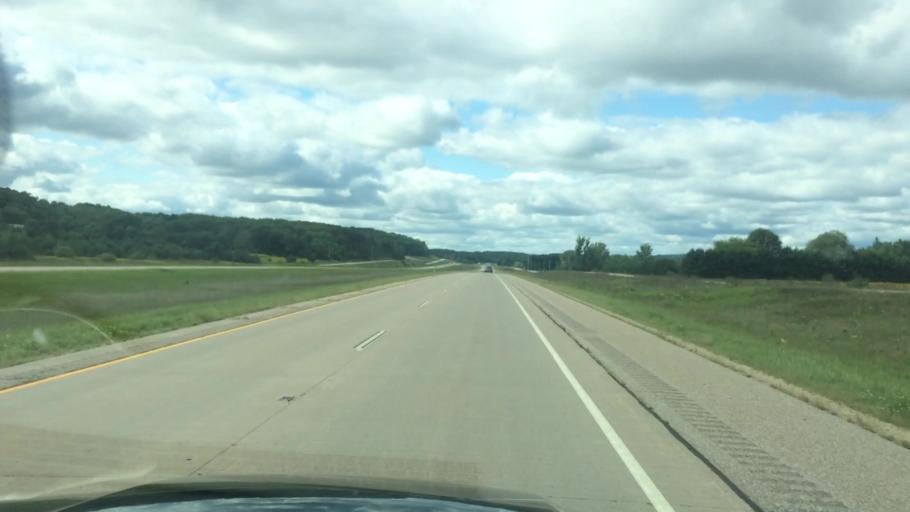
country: US
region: Wisconsin
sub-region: Waupaca County
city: King
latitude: 44.3673
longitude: -89.1410
